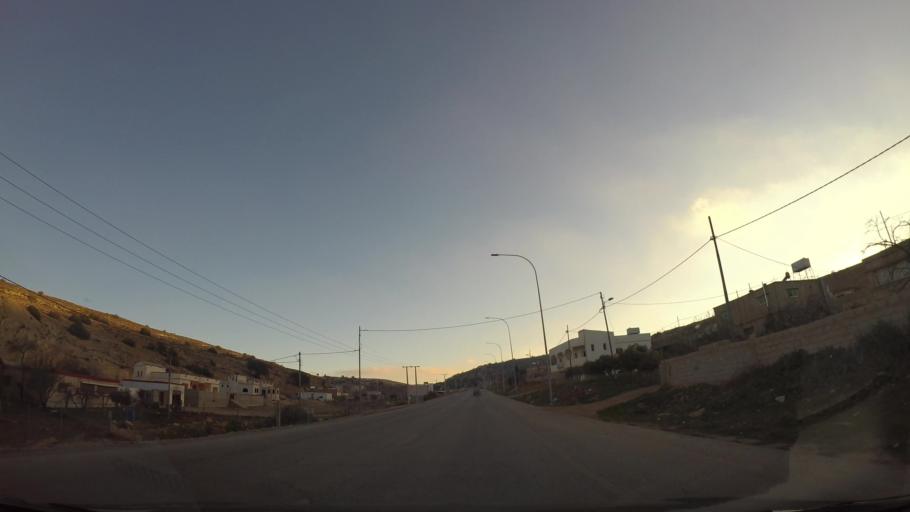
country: JO
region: Ma'an
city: Petra
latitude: 30.4198
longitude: 35.5108
